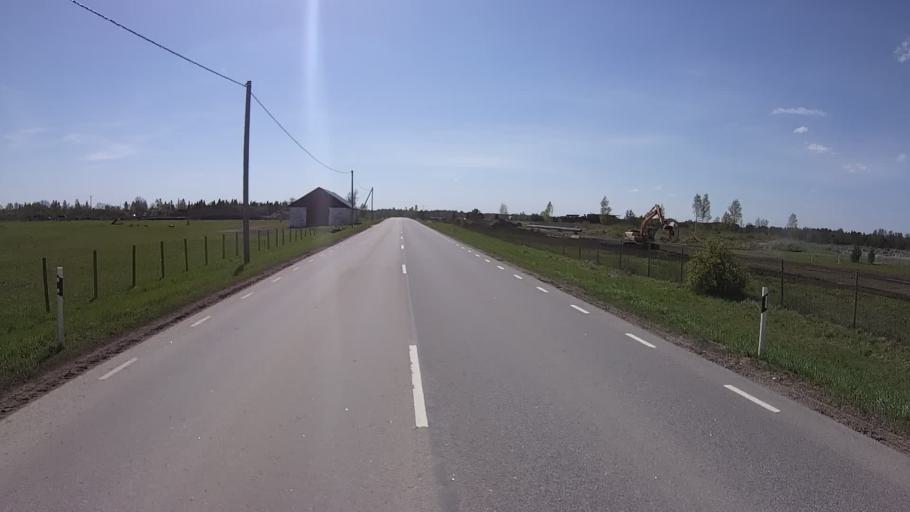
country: EE
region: Harju
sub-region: Keila linn
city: Keila
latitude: 59.3207
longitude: 24.3224
